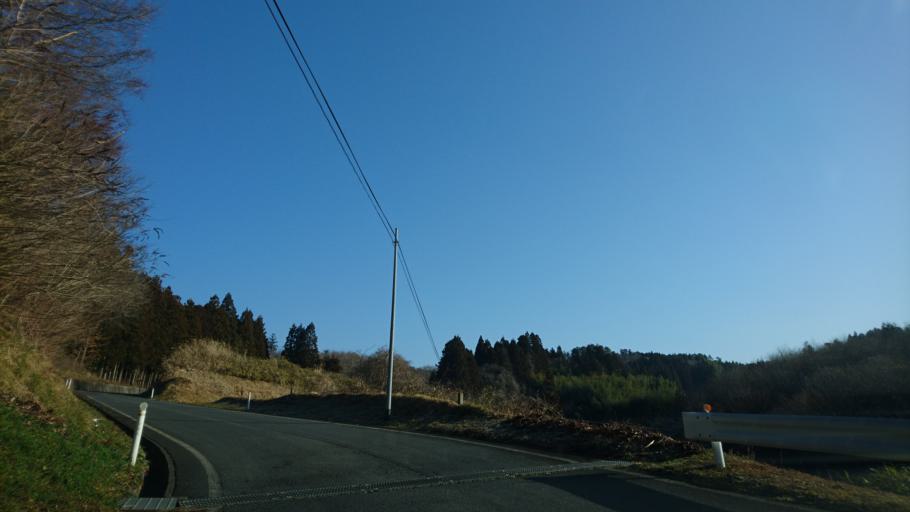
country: JP
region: Iwate
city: Ichinoseki
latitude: 38.9150
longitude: 141.2848
